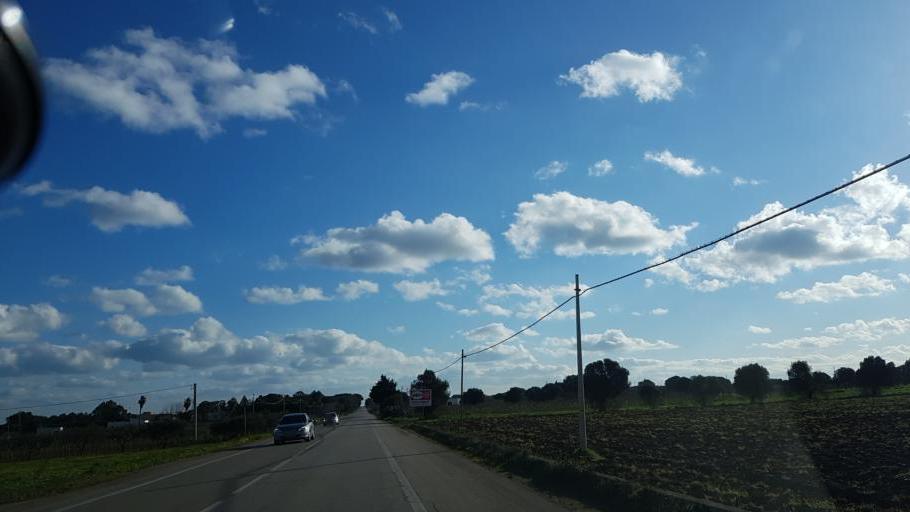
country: IT
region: Apulia
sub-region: Provincia di Brindisi
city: Brindisi
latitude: 40.6467
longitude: 17.8885
